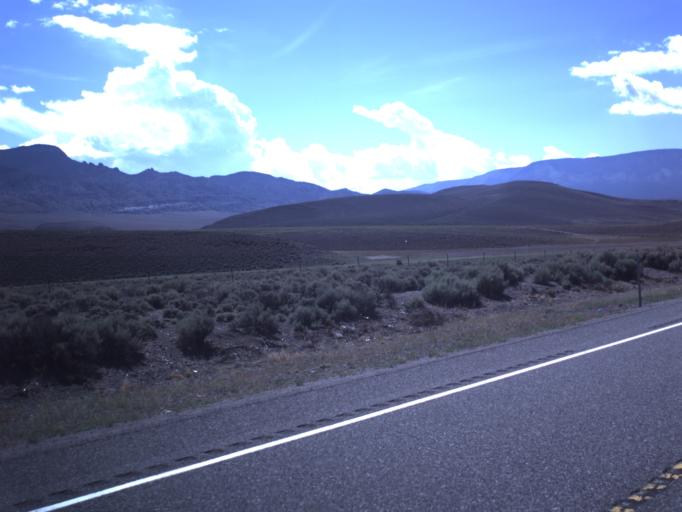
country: US
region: Utah
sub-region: Piute County
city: Junction
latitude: 38.2822
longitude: -112.2246
